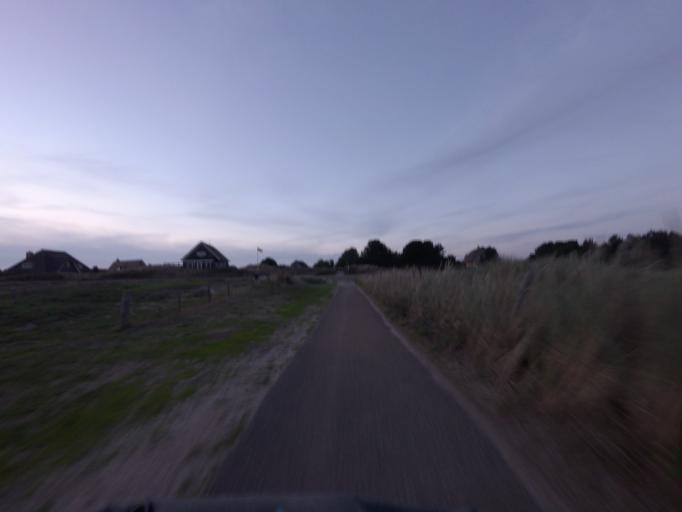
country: NL
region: Friesland
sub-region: Gemeente Ameland
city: Nes
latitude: 53.4551
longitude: 5.7960
